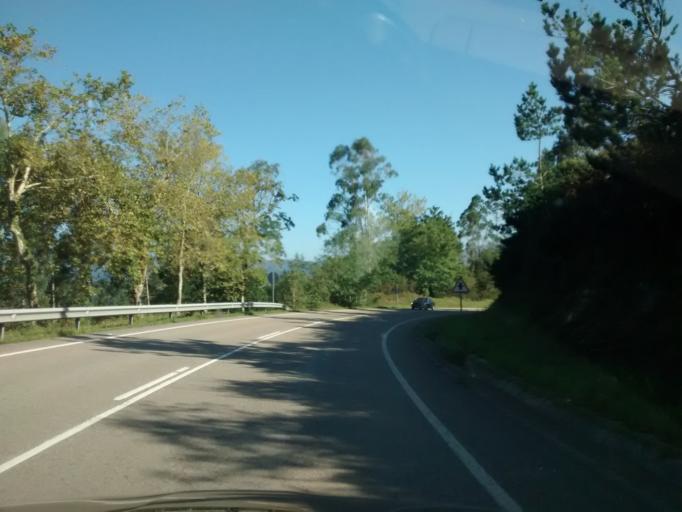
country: ES
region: Cantabria
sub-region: Provincia de Cantabria
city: Cabezon de la Sal
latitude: 43.3276
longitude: -4.2611
